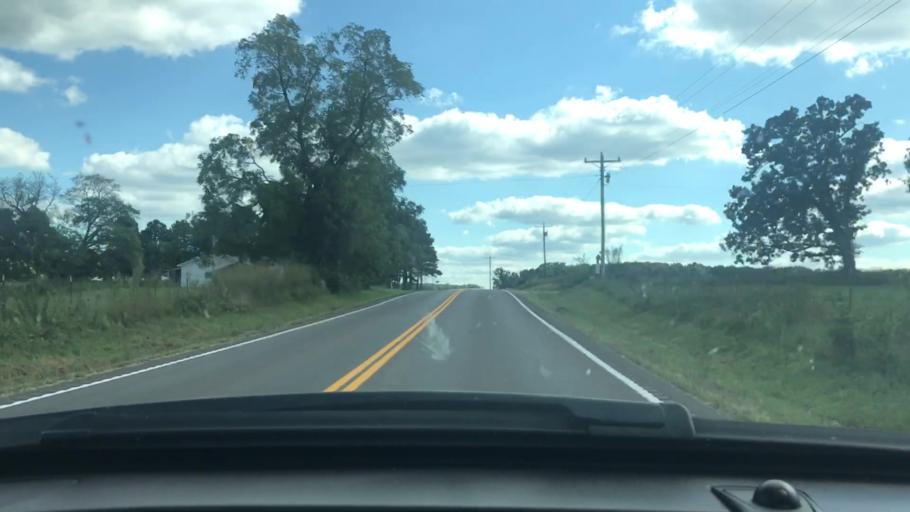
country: US
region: Missouri
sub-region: Wright County
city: Mountain Grove
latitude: 37.2367
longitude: -92.3006
